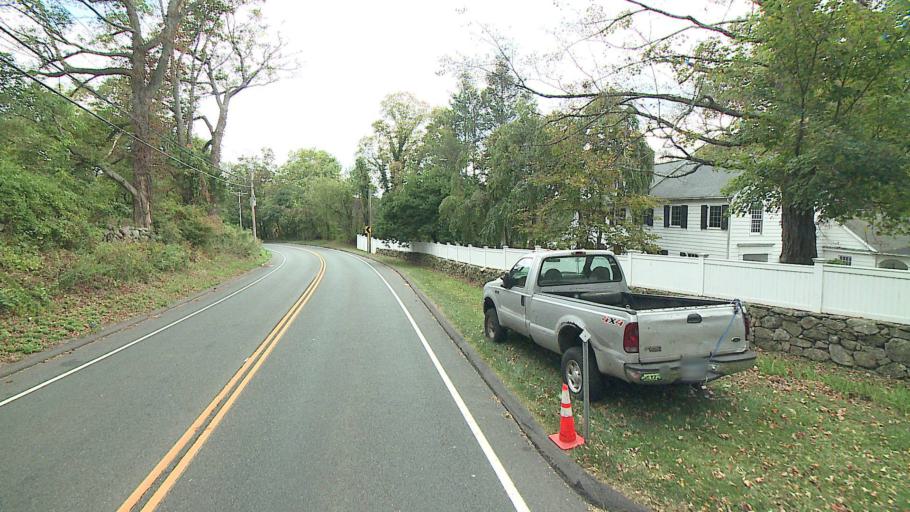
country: US
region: Connecticut
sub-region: Fairfield County
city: Wilton
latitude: 41.2152
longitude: -73.4747
